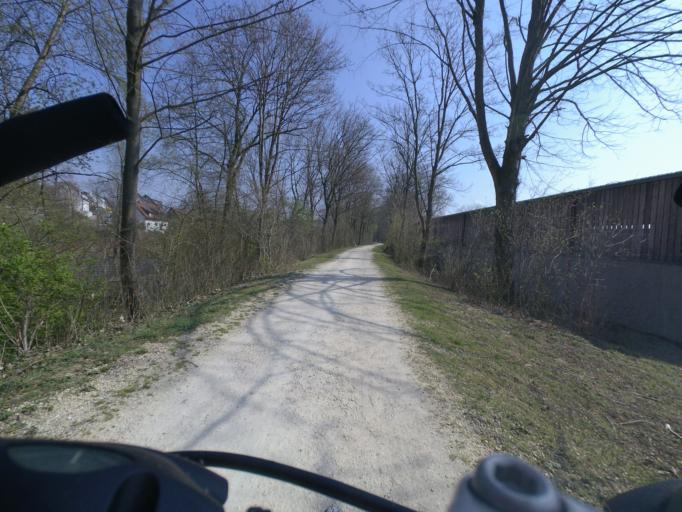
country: DE
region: Baden-Wuerttemberg
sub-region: Regierungsbezirk Stuttgart
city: Nurtingen
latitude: 48.6401
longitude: 9.3395
